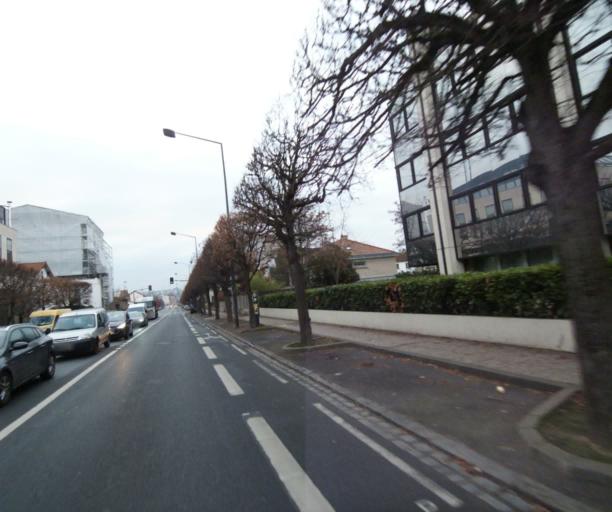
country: FR
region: Ile-de-France
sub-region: Departement des Hauts-de-Seine
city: Rueil-Malmaison
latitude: 48.8861
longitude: 2.1755
